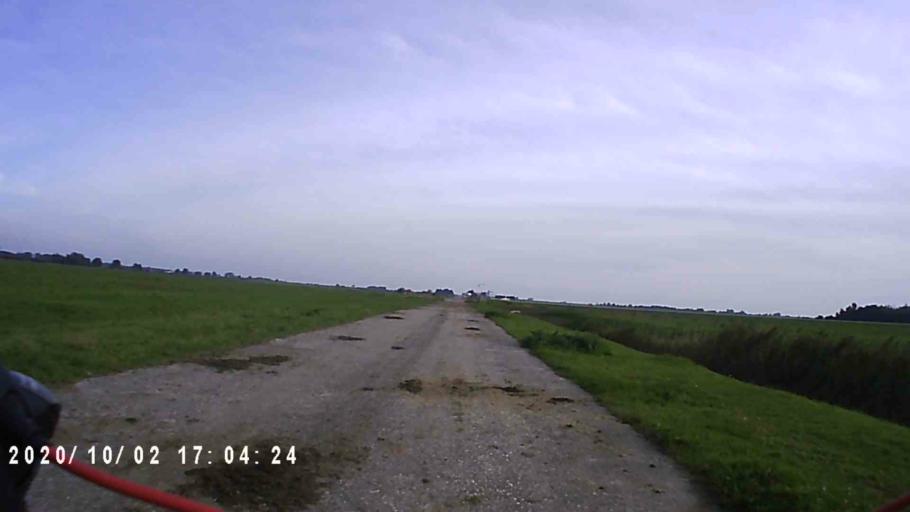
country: NL
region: Groningen
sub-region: Gemeente De Marne
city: Ulrum
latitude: 53.3399
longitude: 6.2674
